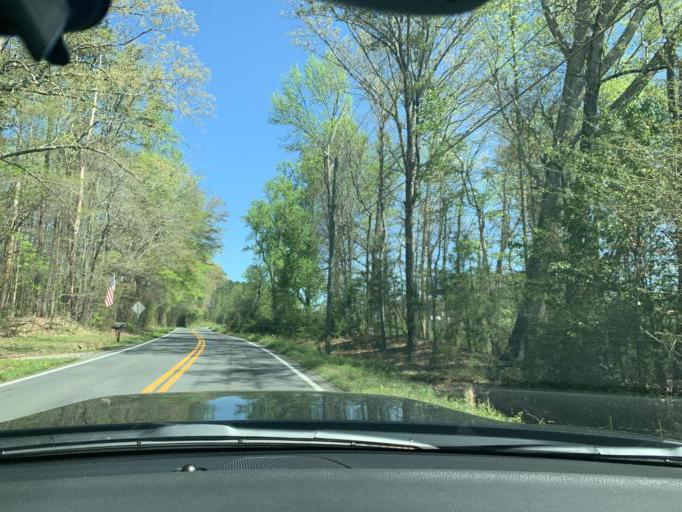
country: US
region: Georgia
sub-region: Forsyth County
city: Cumming
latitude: 34.1506
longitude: -84.1971
